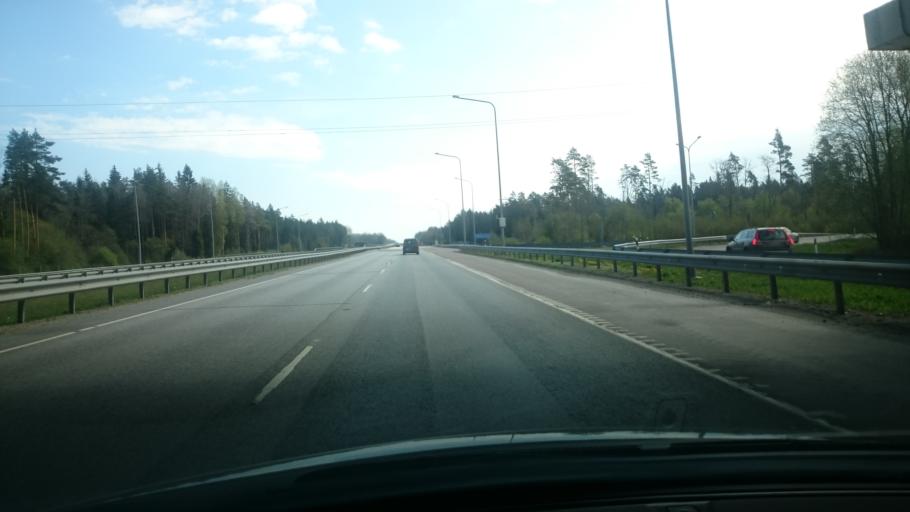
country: EE
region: Harju
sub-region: Raasiku vald
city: Raasiku
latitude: 59.4347
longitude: 25.1908
